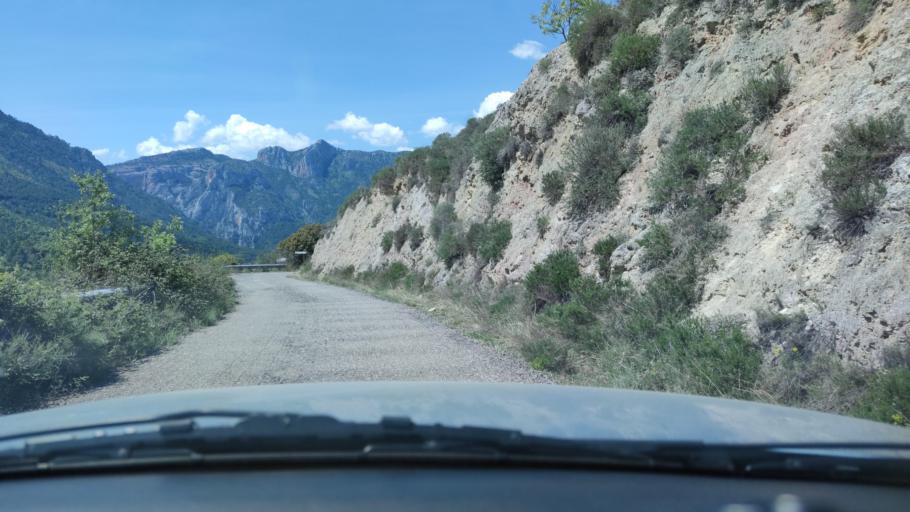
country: ES
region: Catalonia
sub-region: Provincia de Lleida
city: Sort
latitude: 42.3108
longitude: 1.0729
